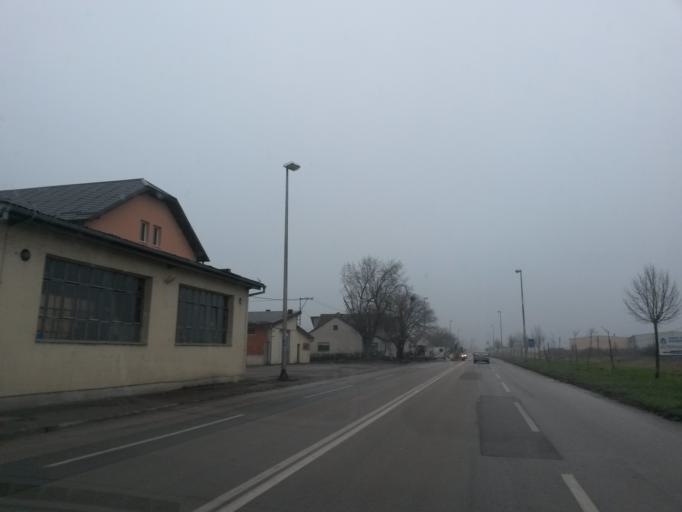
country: HR
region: Vukovarsko-Srijemska
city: Zupanja
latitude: 45.0923
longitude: 18.6972
